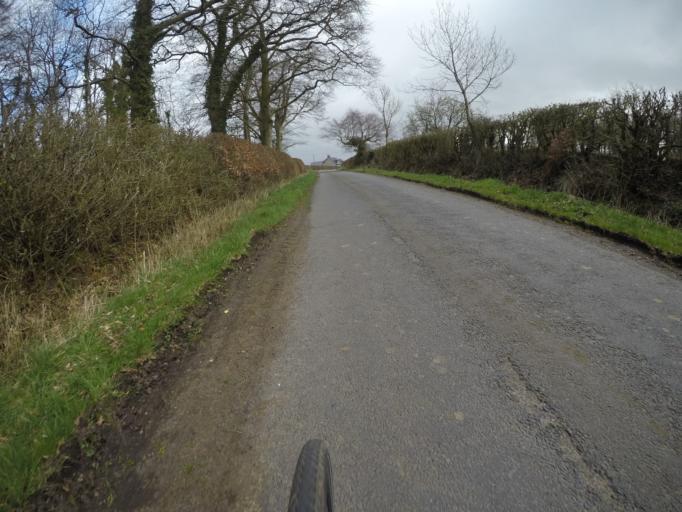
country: GB
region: Scotland
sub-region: East Ayrshire
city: Kilmaurs
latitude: 55.6713
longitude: -4.5661
